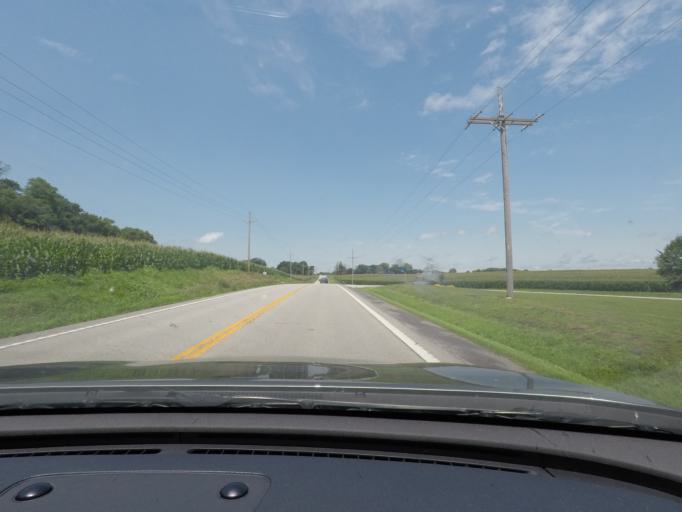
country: US
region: Missouri
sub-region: Saline County
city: Marshall
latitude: 39.1415
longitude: -93.2362
